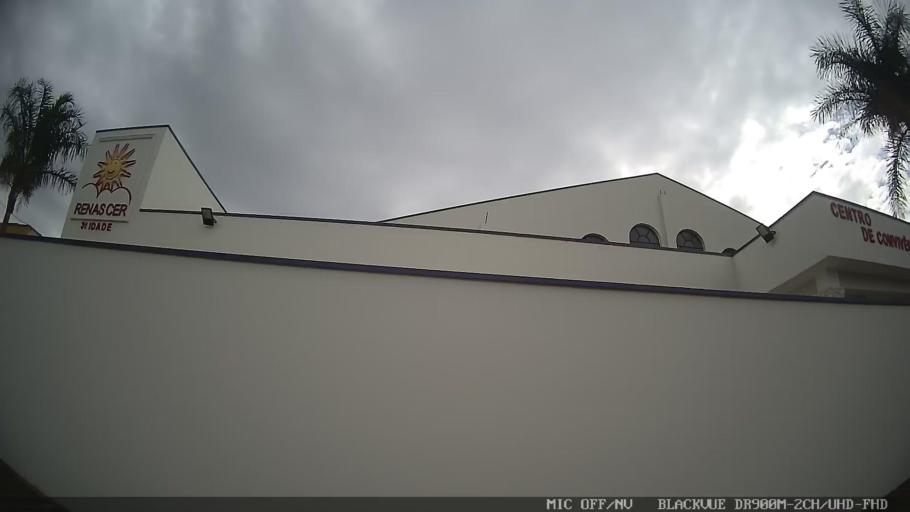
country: BR
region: Sao Paulo
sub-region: Salto
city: Salto
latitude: -23.1971
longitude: -47.2827
